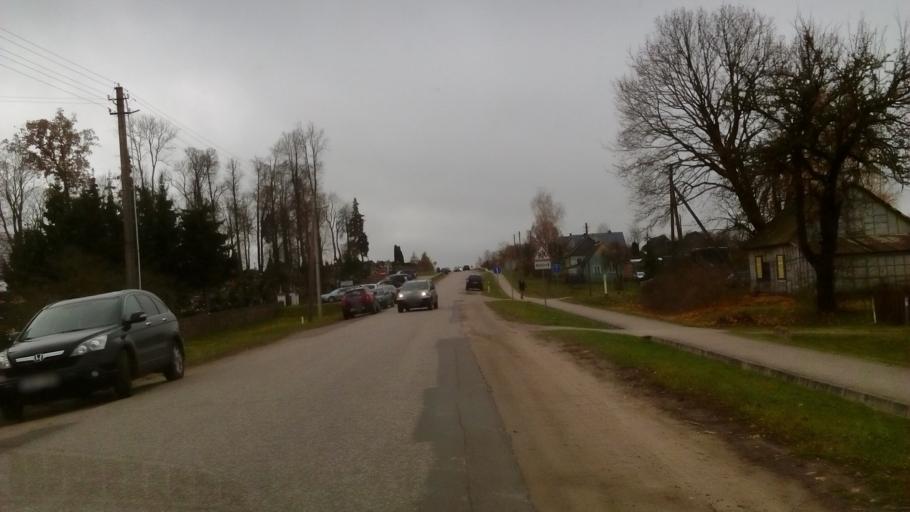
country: LT
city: Simnas
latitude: 54.3778
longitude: 23.5297
